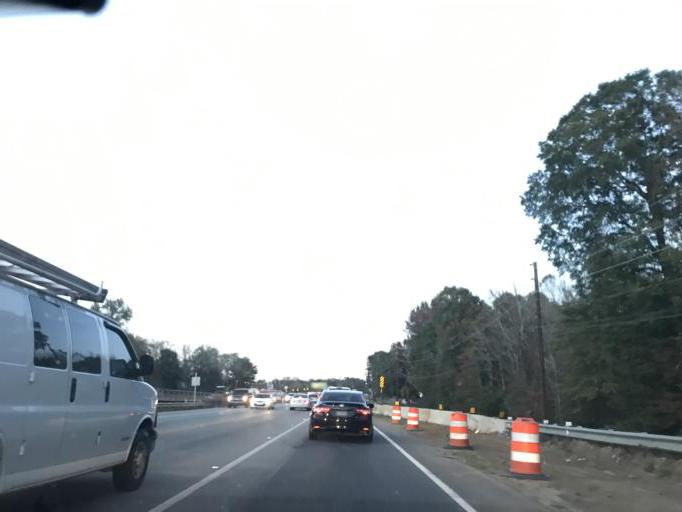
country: US
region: Georgia
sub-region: Bibb County
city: Macon
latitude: 32.7682
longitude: -83.6600
